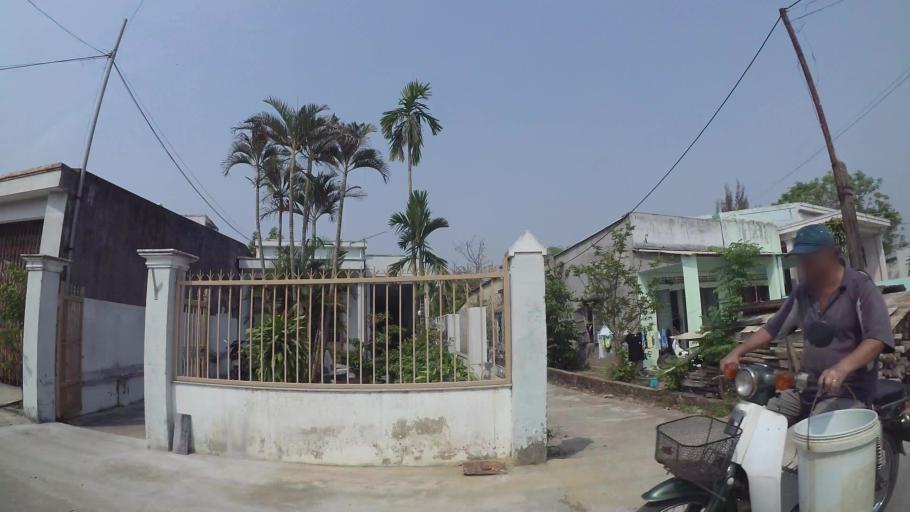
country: VN
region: Da Nang
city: Ngu Hanh Son
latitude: 15.9975
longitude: 108.2386
